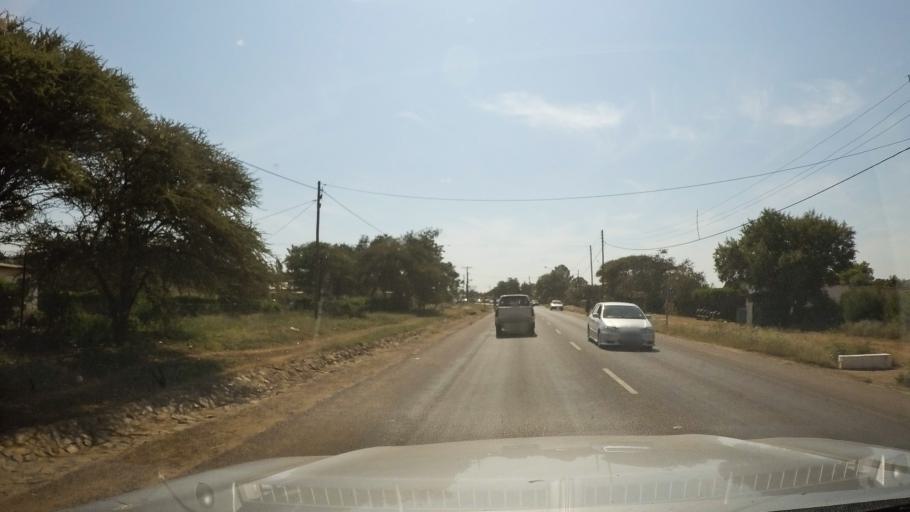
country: BW
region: South East
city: Lobatse
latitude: -25.2069
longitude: 25.6841
